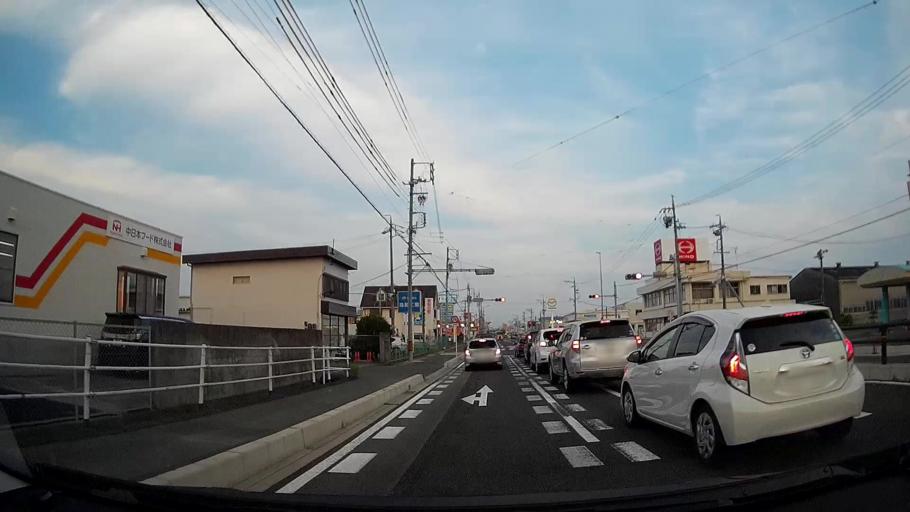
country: JP
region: Aichi
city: Kozakai-cho
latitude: 34.7905
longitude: 137.3733
